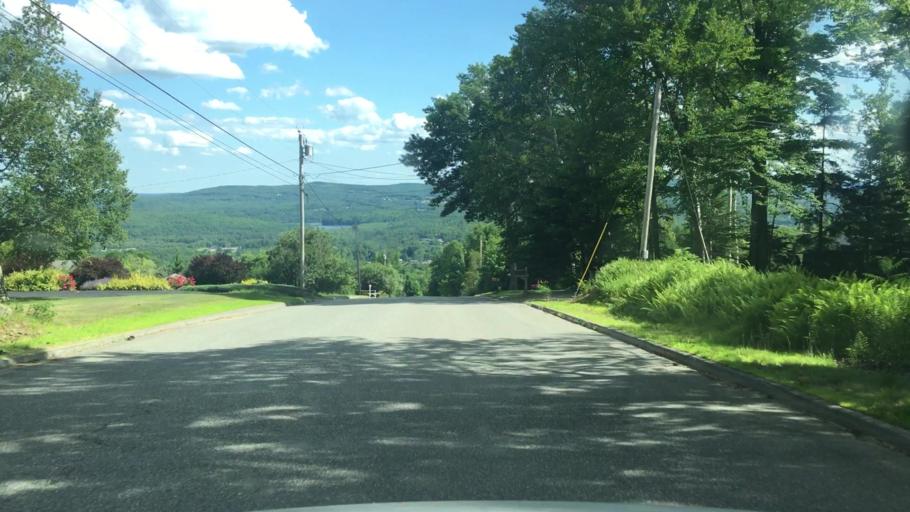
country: US
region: Maine
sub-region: Franklin County
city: Wilton
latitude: 44.6337
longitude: -70.1980
